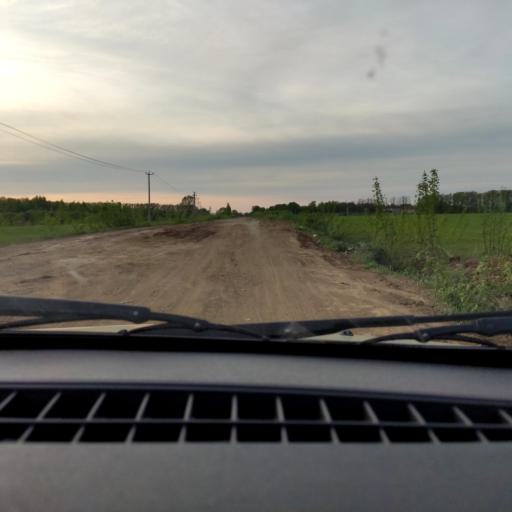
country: RU
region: Bashkortostan
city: Iglino
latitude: 54.8506
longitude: 56.3998
